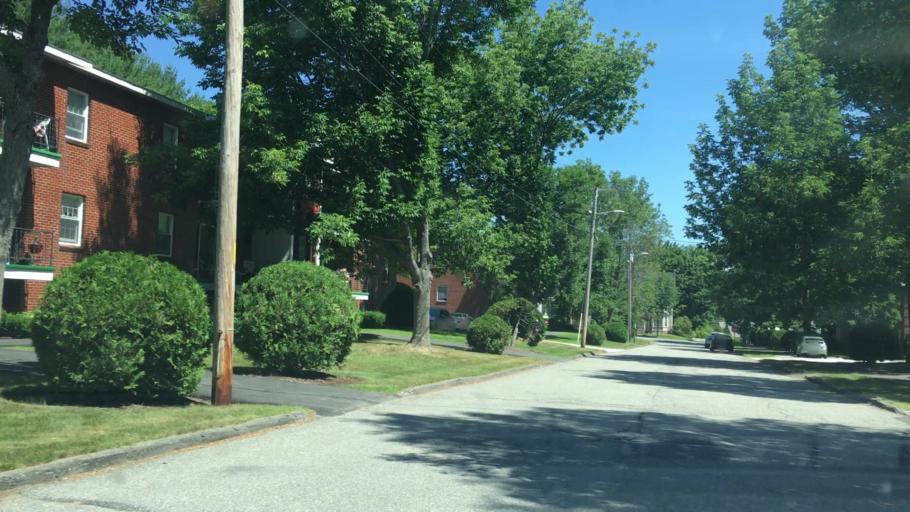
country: US
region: Maine
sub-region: Penobscot County
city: Bangor
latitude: 44.8099
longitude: -68.7973
